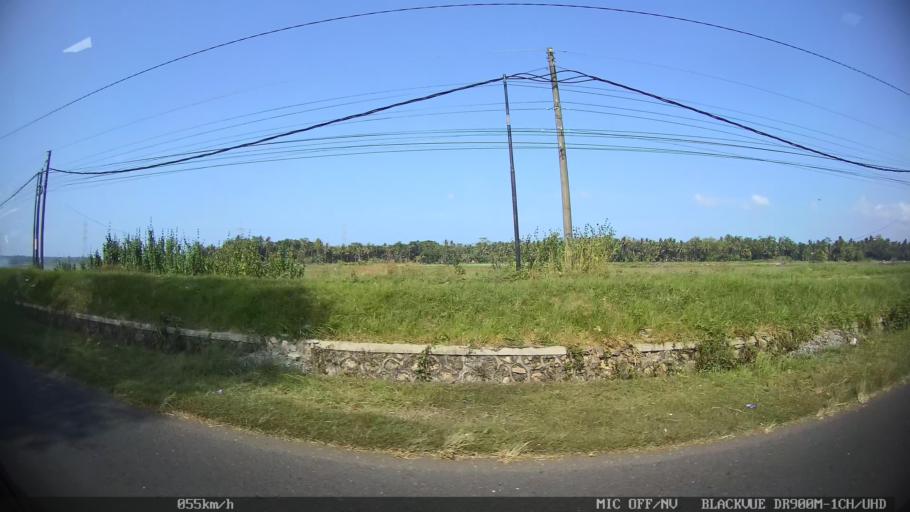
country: ID
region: Daerah Istimewa Yogyakarta
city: Srandakan
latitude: -7.9130
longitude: 110.1766
